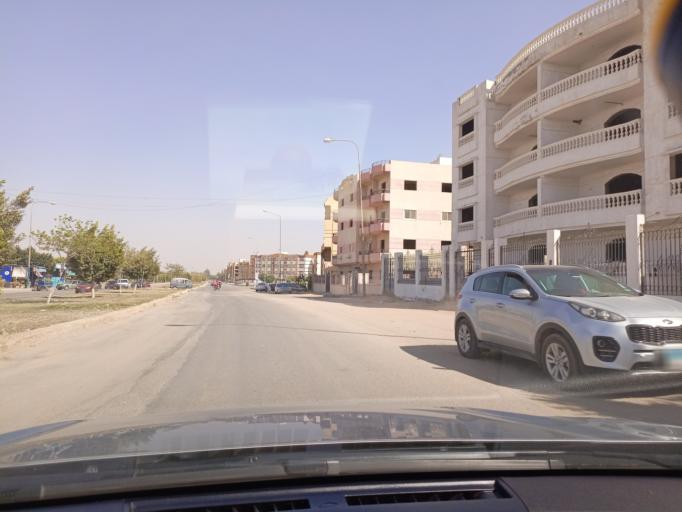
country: EG
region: Muhafazat al Qalyubiyah
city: Al Khankah
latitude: 30.2276
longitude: 31.4463
